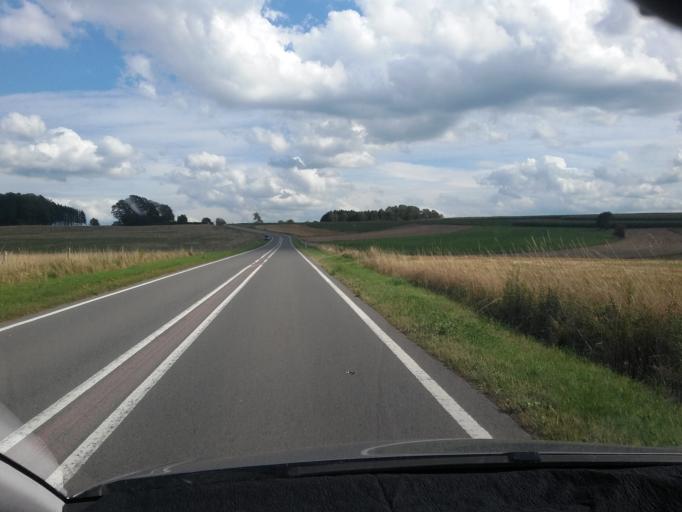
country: BE
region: Wallonia
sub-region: Province du Luxembourg
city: Saint-Hubert
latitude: 50.0314
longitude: 5.3307
